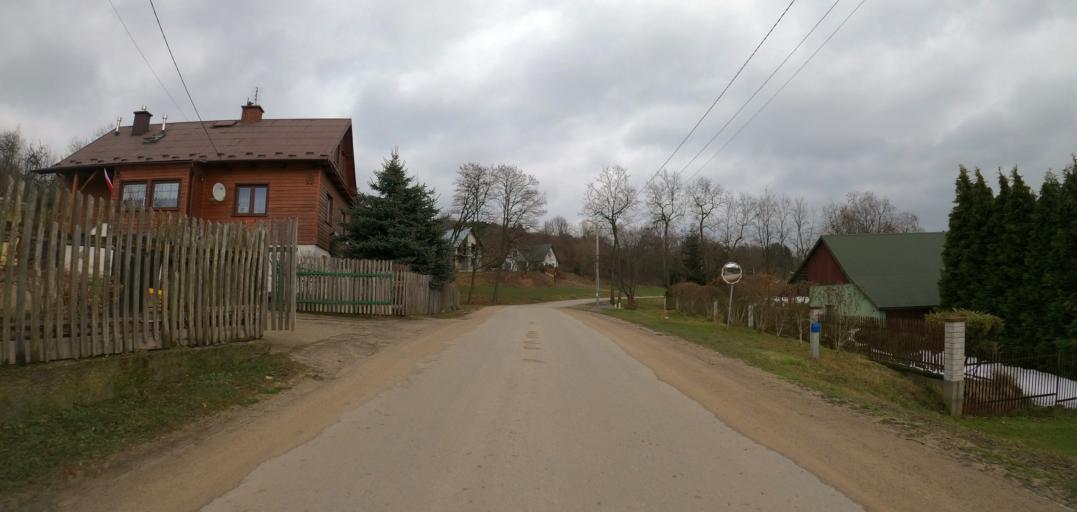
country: PL
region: Subcarpathian Voivodeship
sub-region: Powiat debicki
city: Pilzno
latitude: 49.9881
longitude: 21.3354
